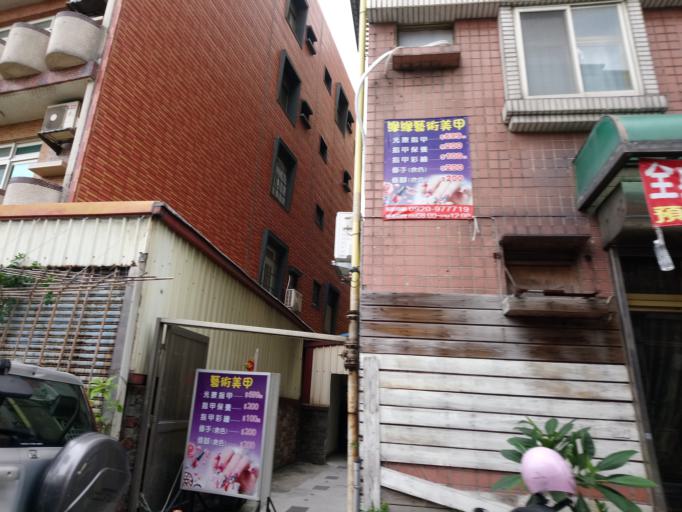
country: TW
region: Taiwan
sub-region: Hsinchu
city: Hsinchu
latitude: 24.8085
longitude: 120.9574
